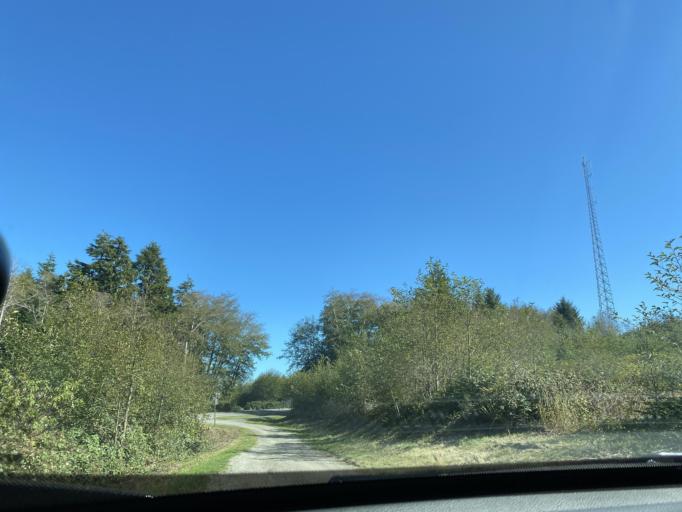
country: US
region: Washington
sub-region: Clallam County
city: Forks
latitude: 47.8983
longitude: -124.6190
